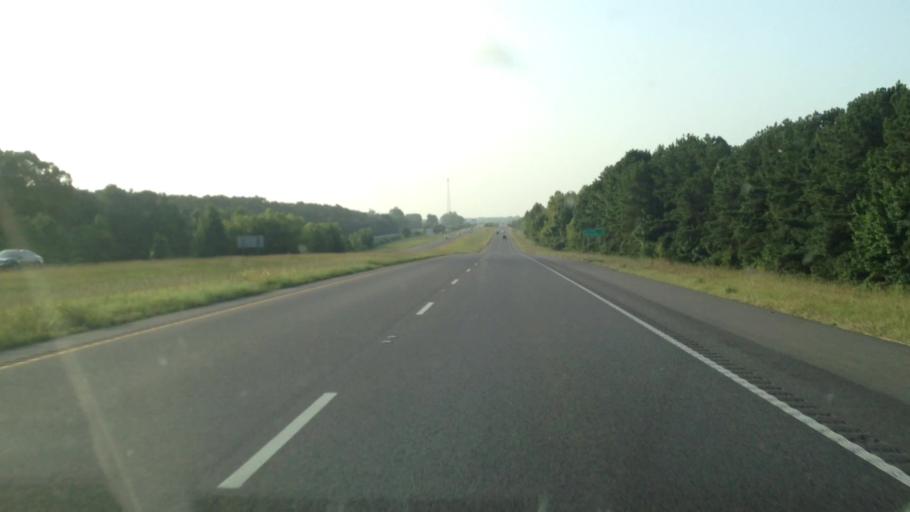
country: US
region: Louisiana
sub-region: Rapides Parish
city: Boyce
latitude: 31.4012
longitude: -92.7053
